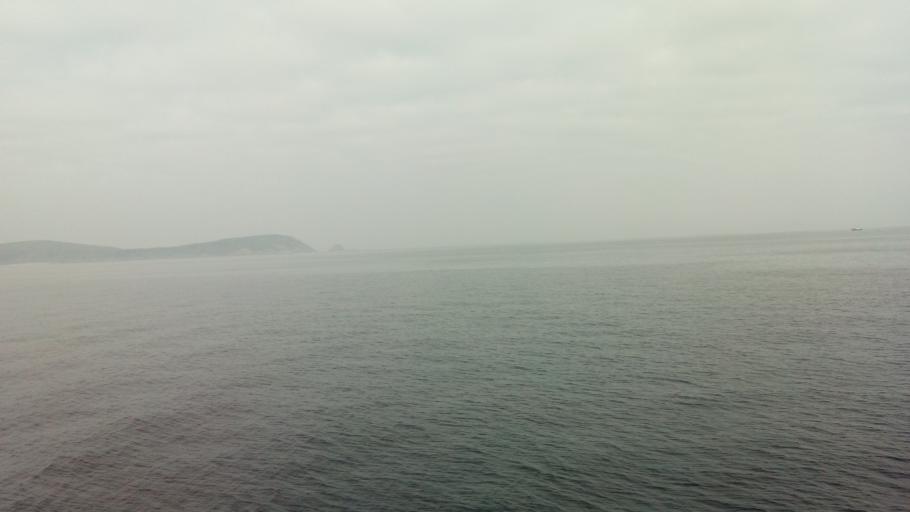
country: ES
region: Galicia
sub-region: Provincia de Pontevedra
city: Sanxenxo
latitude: 42.3797
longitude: -8.8865
